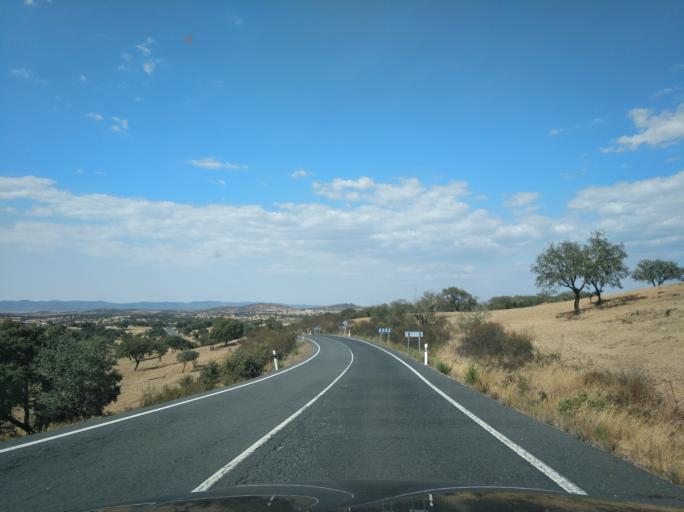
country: ES
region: Andalusia
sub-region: Provincia de Huelva
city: Cabezas Rubias
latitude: 37.6819
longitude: -7.1066
